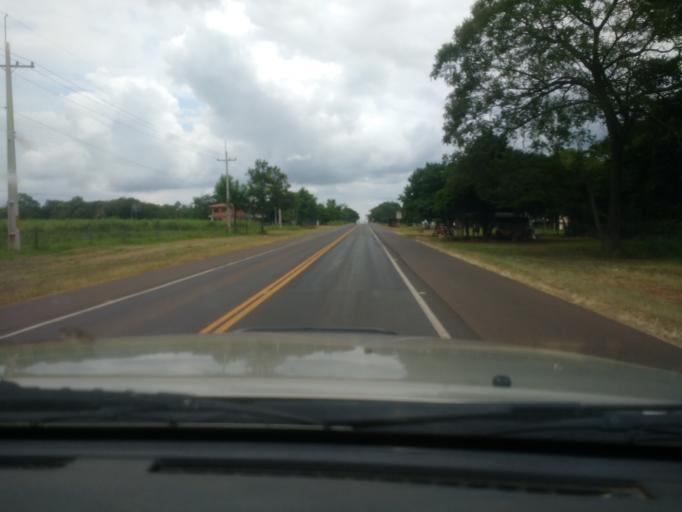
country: PY
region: Cordillera
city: Arroyos y Esteros
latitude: -25.0562
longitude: -57.1309
